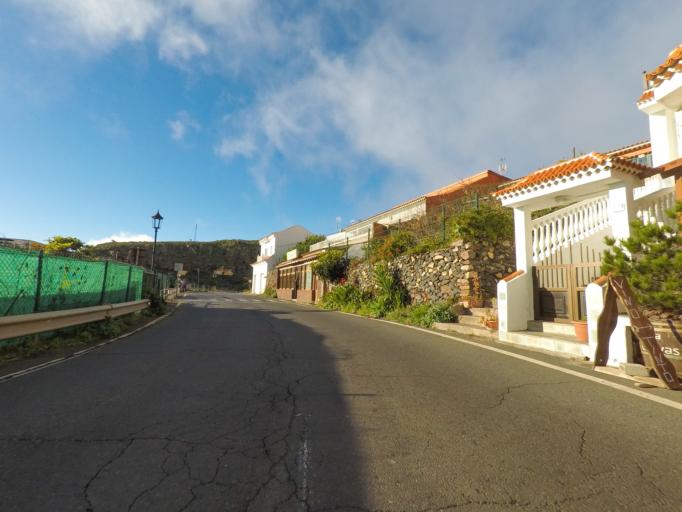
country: ES
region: Canary Islands
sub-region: Provincia de Santa Cruz de Tenerife
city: Vallehermosa
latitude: 28.1312
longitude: -17.3206
